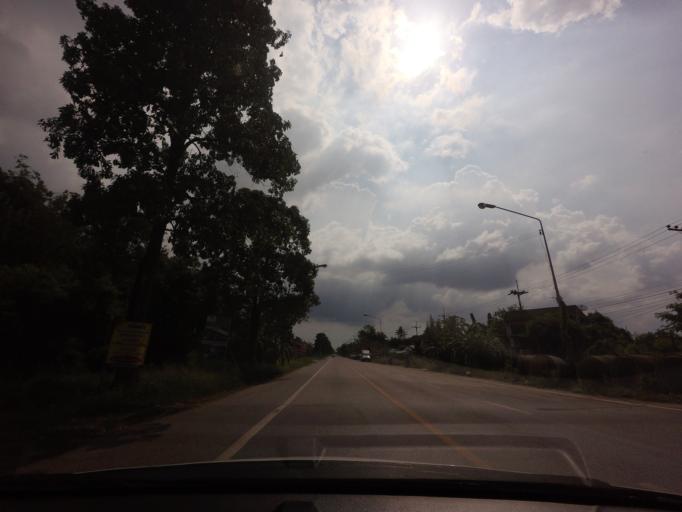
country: TH
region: Nakhon Pathom
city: Nakhon Chai Si
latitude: 13.7787
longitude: 100.2321
